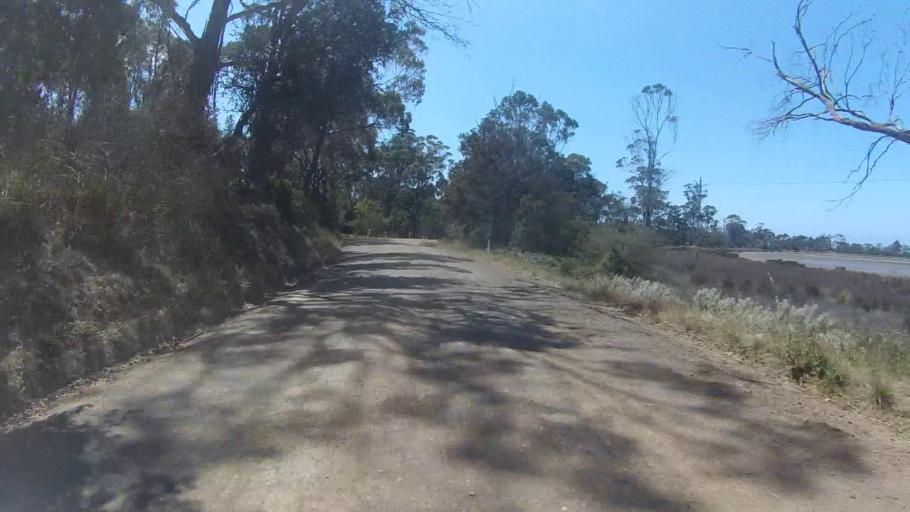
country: AU
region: Tasmania
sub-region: Sorell
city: Sorell
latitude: -42.8470
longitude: 147.8424
